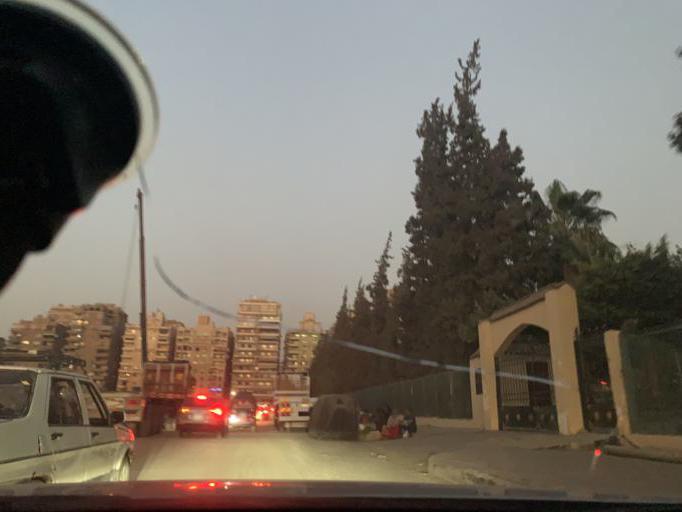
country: EG
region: Muhafazat al Qahirah
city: Cairo
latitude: 30.0631
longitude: 31.3474
